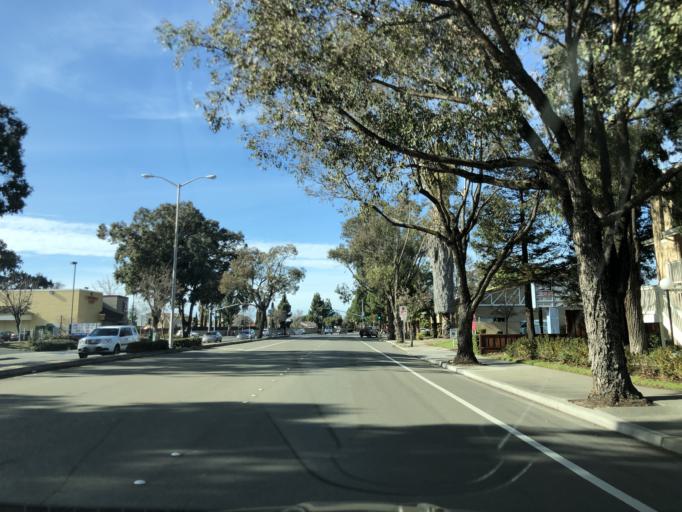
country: US
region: California
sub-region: Alameda County
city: Fremont
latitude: 37.5244
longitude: -122.0065
